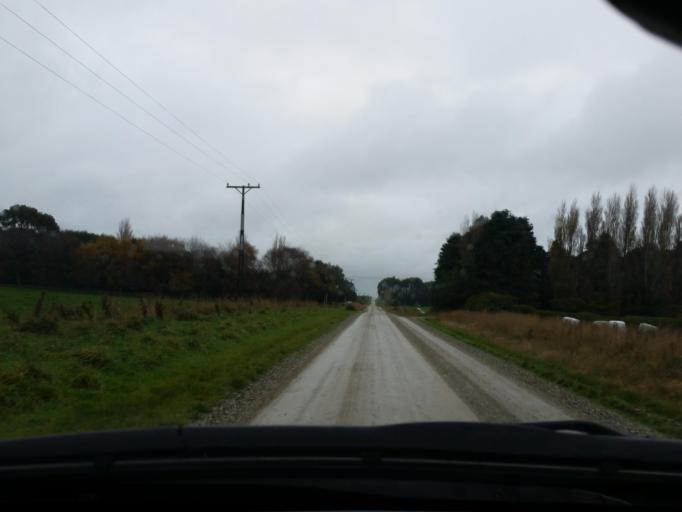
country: NZ
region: Southland
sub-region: Invercargill City
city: Invercargill
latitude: -46.2850
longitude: 168.5001
